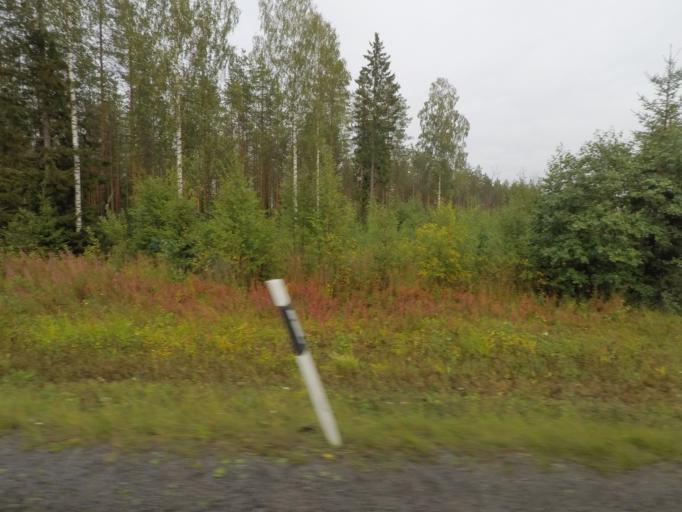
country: FI
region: Southern Savonia
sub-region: Pieksaemaeki
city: Juva
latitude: 62.0334
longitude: 27.7995
